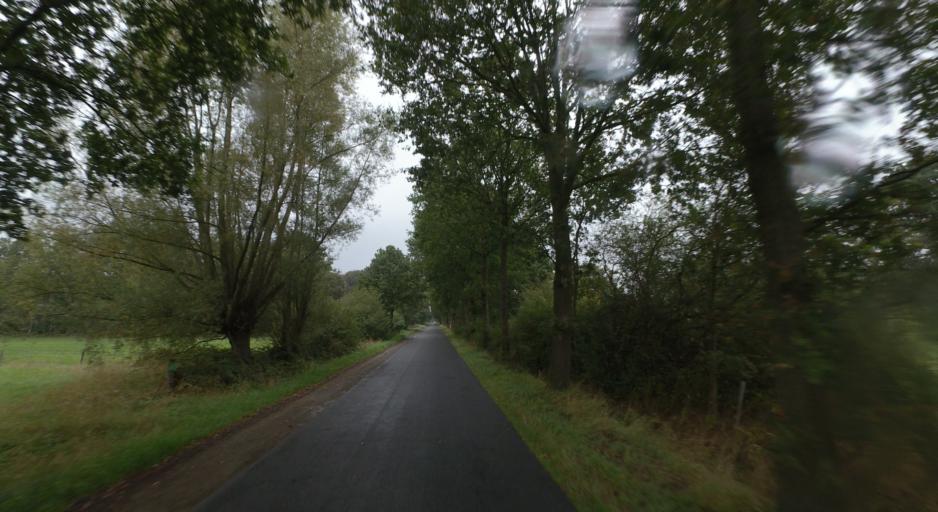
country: DE
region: North Rhine-Westphalia
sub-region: Regierungsbezirk Dusseldorf
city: Hamminkeln
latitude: 51.7166
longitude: 6.6123
